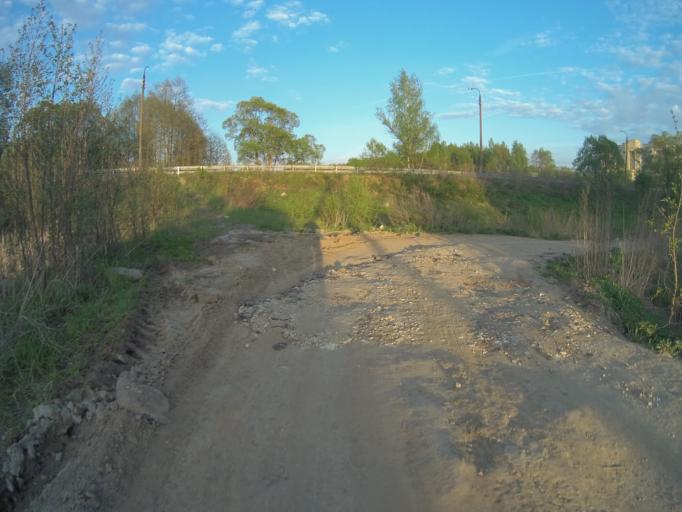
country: RU
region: Vladimir
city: Kommunar
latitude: 56.0652
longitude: 40.4873
